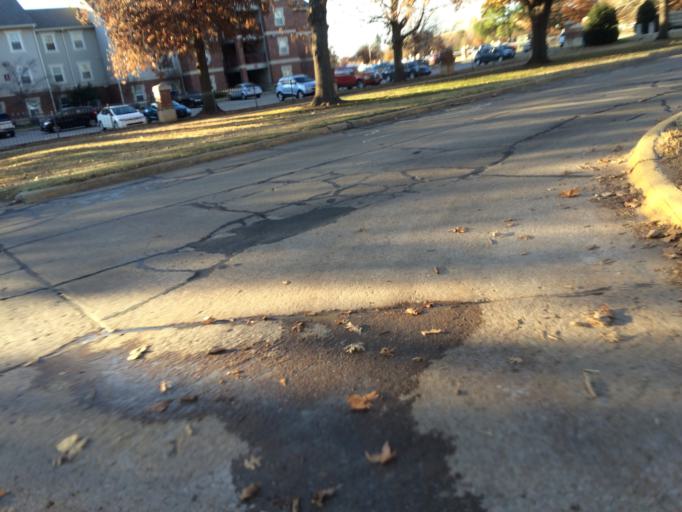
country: US
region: Oklahoma
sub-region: Cleveland County
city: Norman
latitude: 35.1935
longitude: -97.4448
